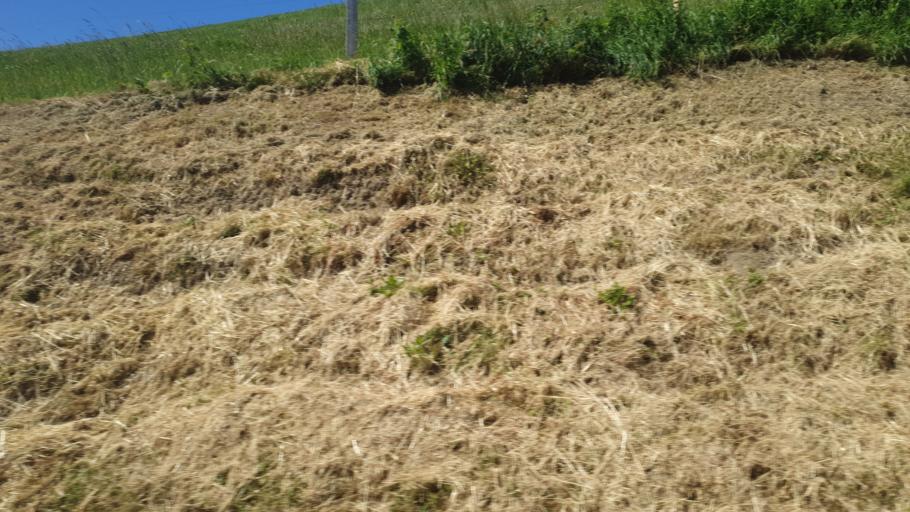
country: CH
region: Fribourg
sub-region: Sarine District
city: Givisiez
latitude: 46.8480
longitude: 7.1374
